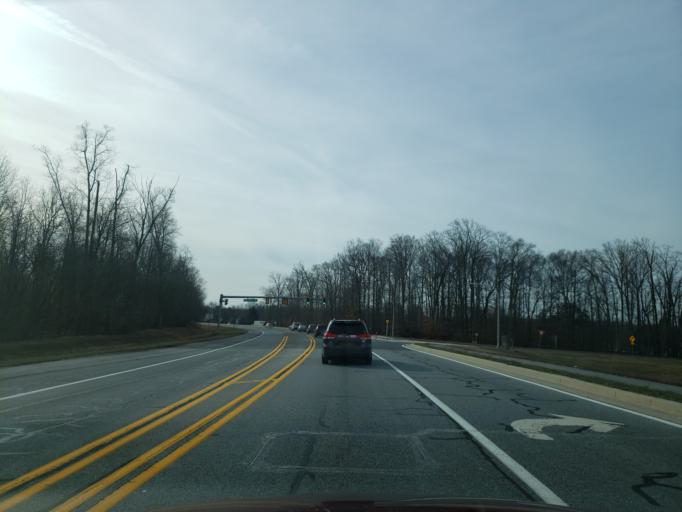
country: US
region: Delaware
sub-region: Kent County
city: Cheswold
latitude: 39.1852
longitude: -75.5609
